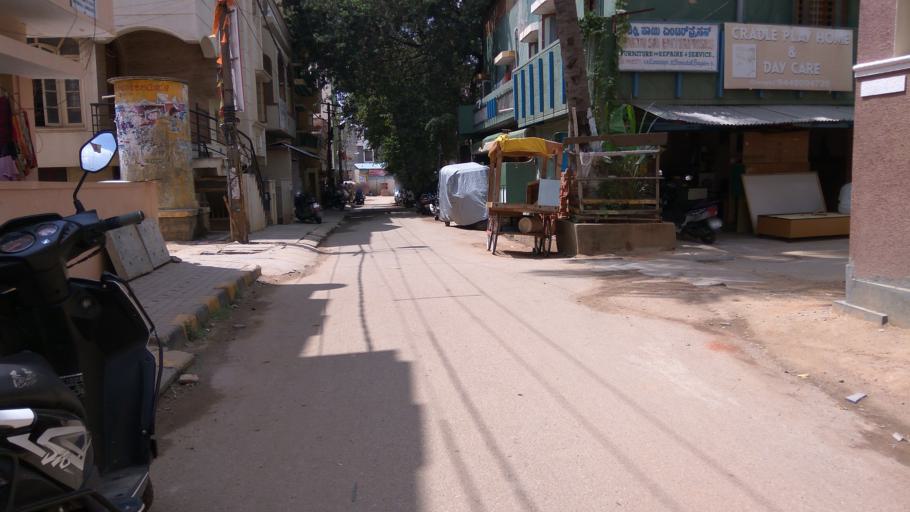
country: IN
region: Karnataka
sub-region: Bangalore Urban
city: Bangalore
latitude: 12.9680
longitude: 77.6392
